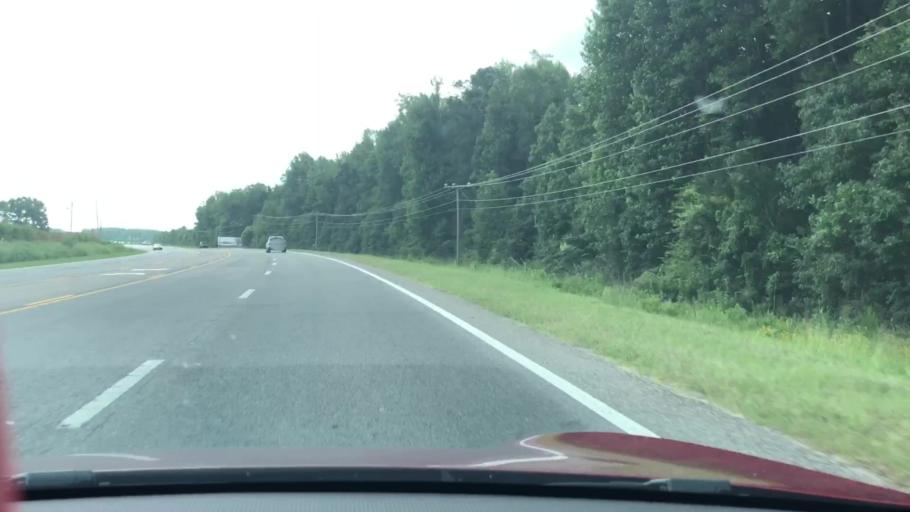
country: US
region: North Carolina
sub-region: Currituck County
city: Currituck
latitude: 36.3207
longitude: -75.9372
